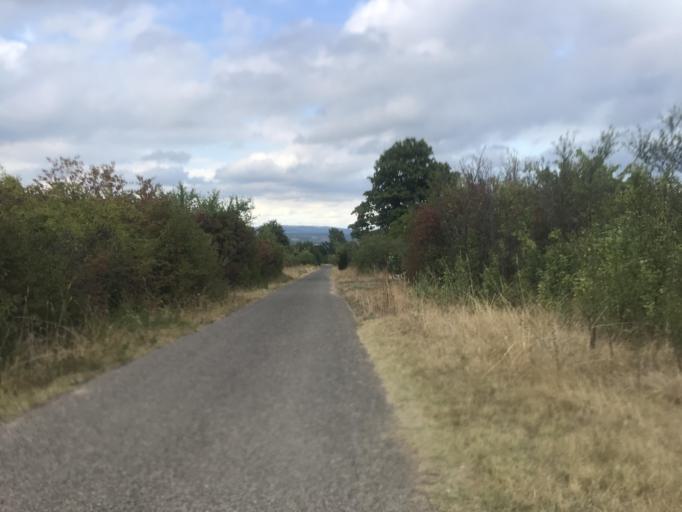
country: DE
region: Rheinland-Pfalz
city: Nieder-Ingelheim
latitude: 49.9860
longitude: 8.0835
